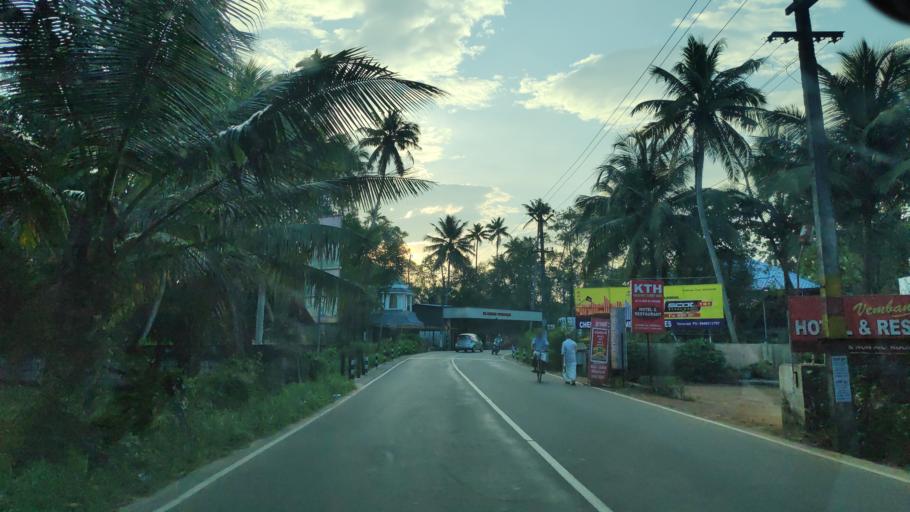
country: IN
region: Kerala
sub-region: Alappuzha
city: Shertallai
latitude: 9.6828
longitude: 76.3594
